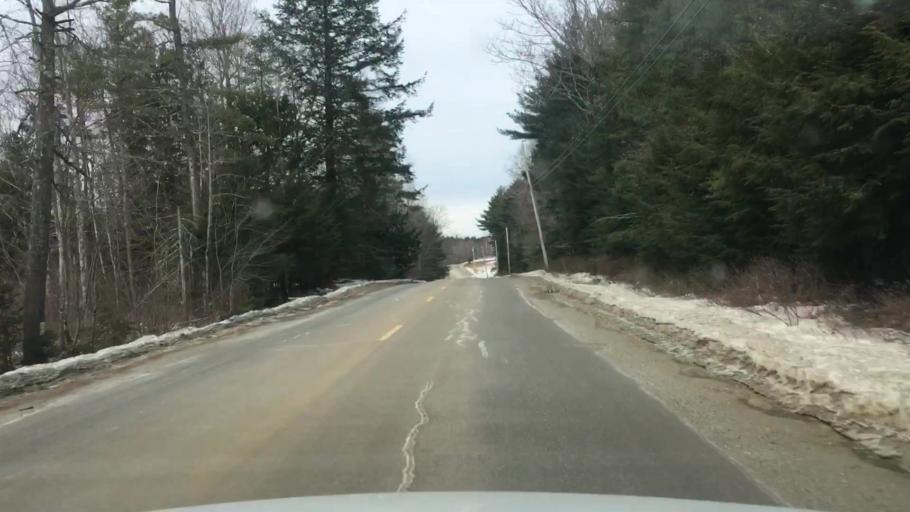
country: US
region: Maine
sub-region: Kennebec County
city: Chelsea
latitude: 44.2629
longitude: -69.6473
